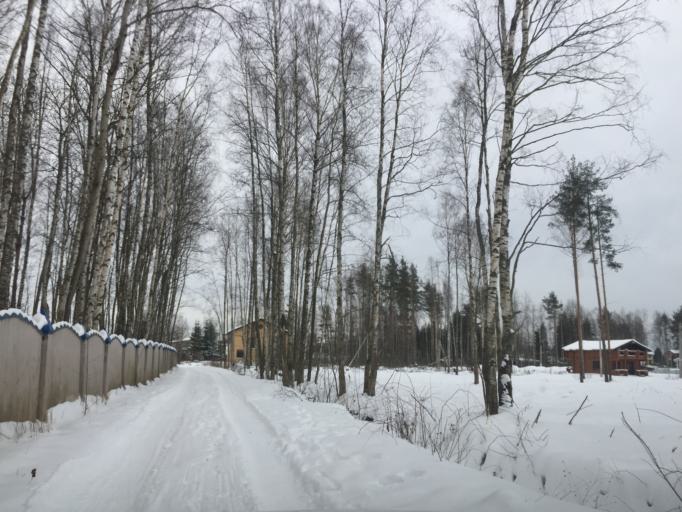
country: RU
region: Leningrad
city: Otradnoye
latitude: 59.7803
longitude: 30.7848
